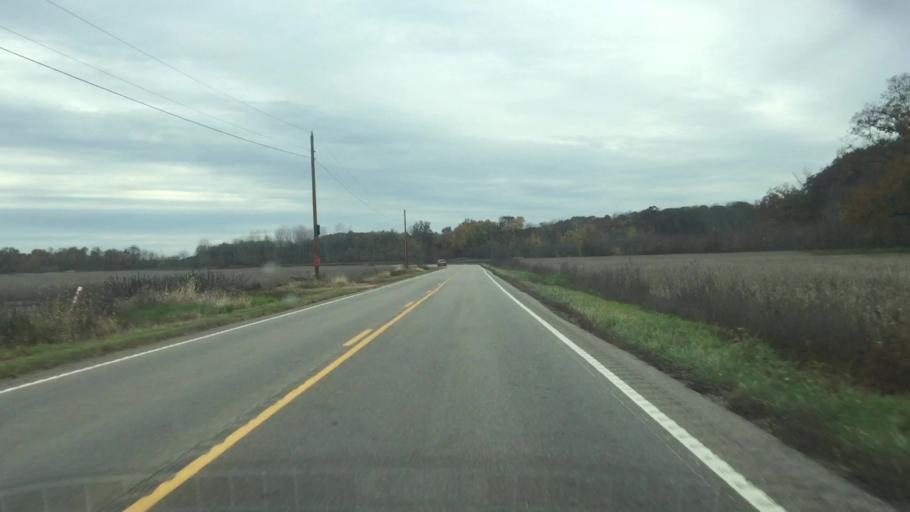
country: US
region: Missouri
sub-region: Callaway County
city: Fulton
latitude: 38.7081
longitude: -91.7507
